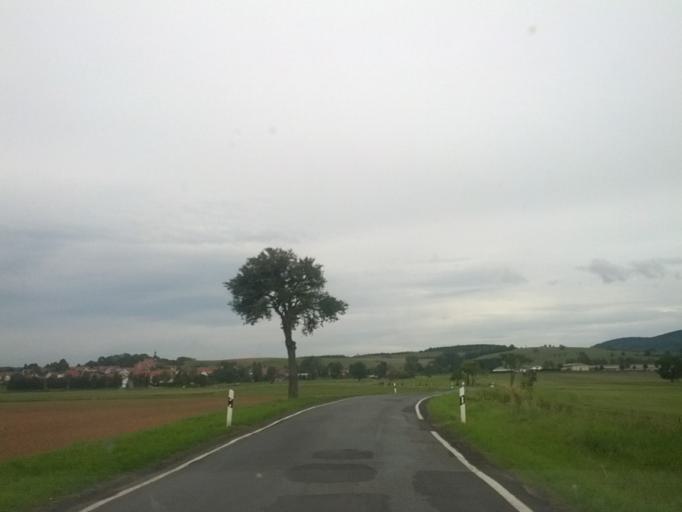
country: DE
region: Thuringia
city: Bad Salzungen
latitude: 50.8537
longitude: 10.2503
